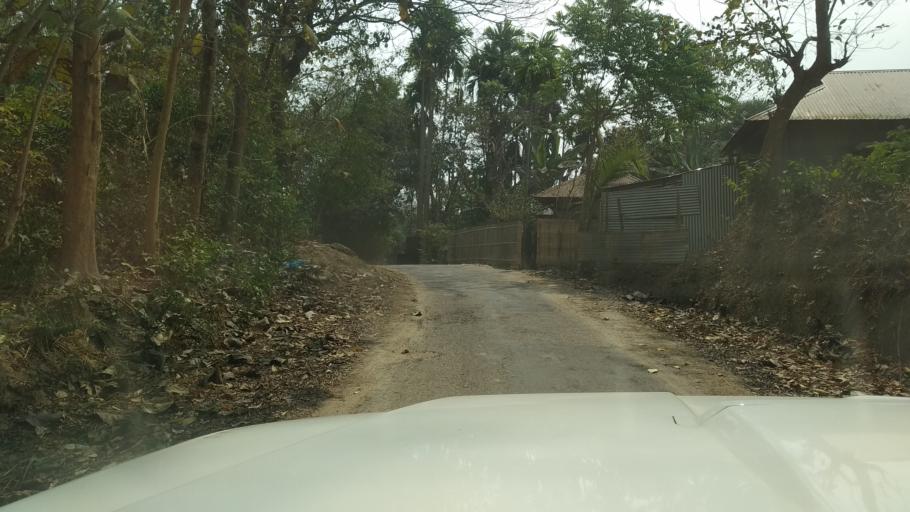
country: IN
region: Tripura
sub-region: West Tripura
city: Sonamura
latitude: 23.4289
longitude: 91.3147
